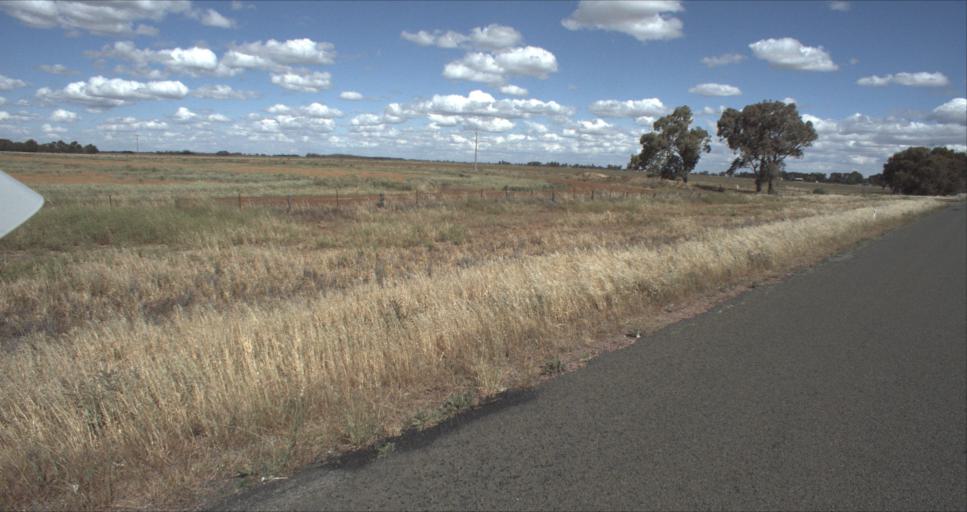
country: AU
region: New South Wales
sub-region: Leeton
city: Leeton
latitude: -34.4701
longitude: 146.2511
